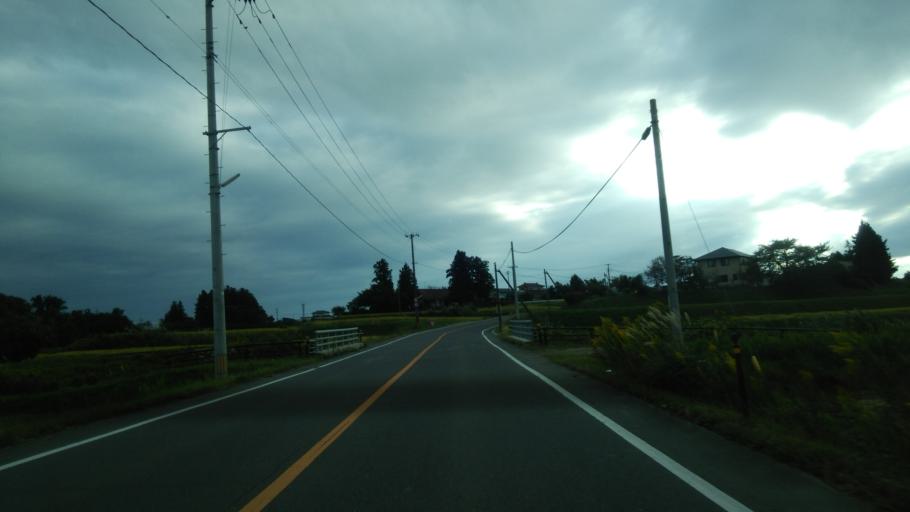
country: JP
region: Fukushima
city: Koriyama
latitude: 37.3500
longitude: 140.3394
